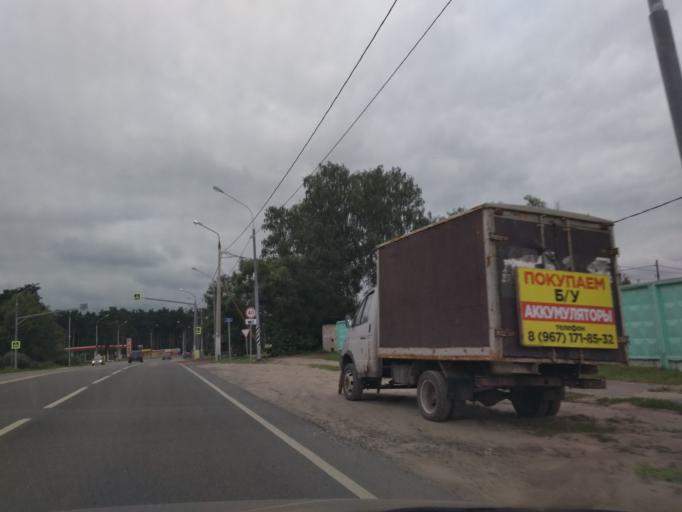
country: RU
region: Moskovskaya
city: Orekhovo-Zuyevo
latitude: 55.8273
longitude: 38.9638
